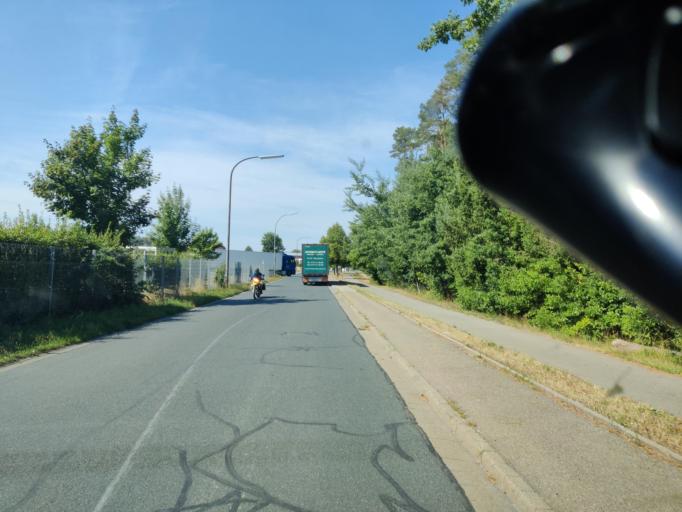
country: DE
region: Bavaria
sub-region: Regierungsbezirk Mittelfranken
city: Hilpoltstein
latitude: 49.1841
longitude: 11.1809
